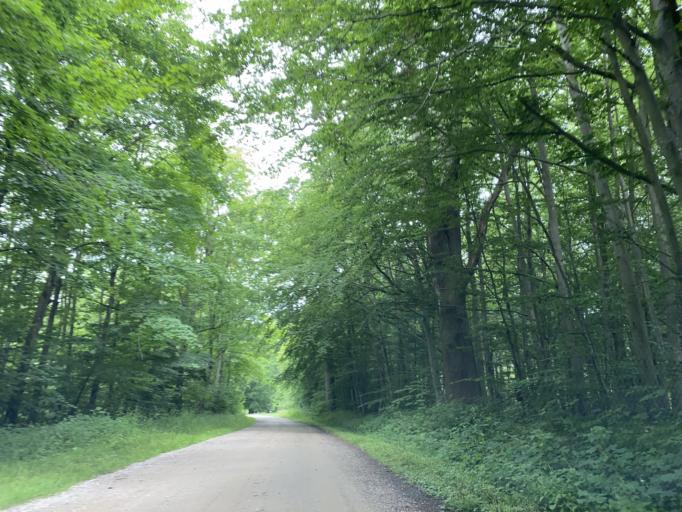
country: DK
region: South Denmark
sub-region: Sonderborg Kommune
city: Sonderborg
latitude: 54.9022
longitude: 9.8374
